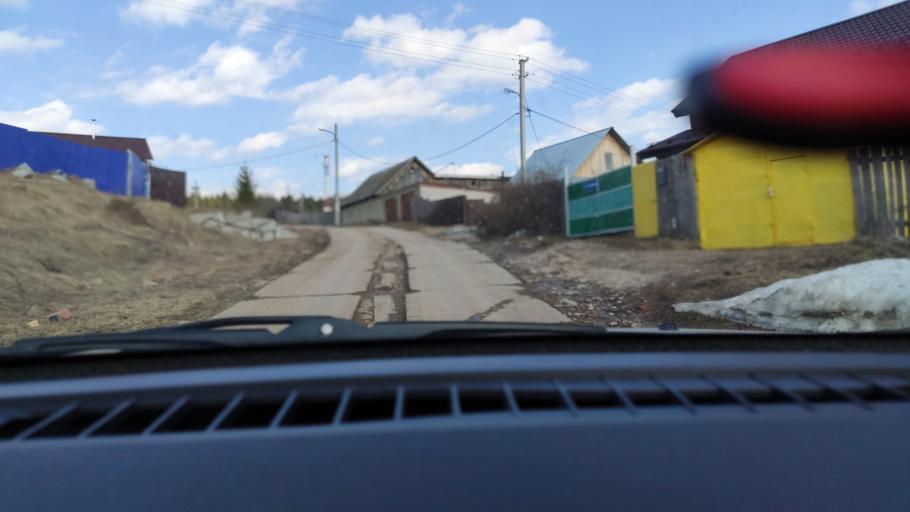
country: RU
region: Perm
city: Ferma
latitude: 57.9621
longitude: 56.3728
